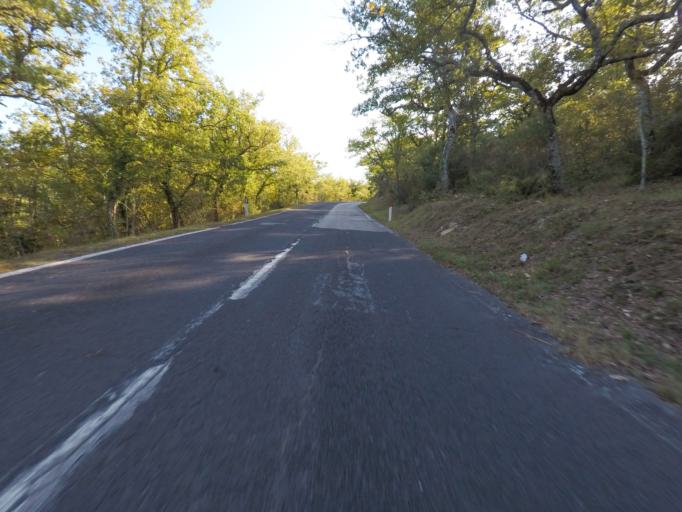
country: IT
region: Tuscany
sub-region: Provincia di Siena
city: Radda in Chianti
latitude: 43.4590
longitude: 11.3869
